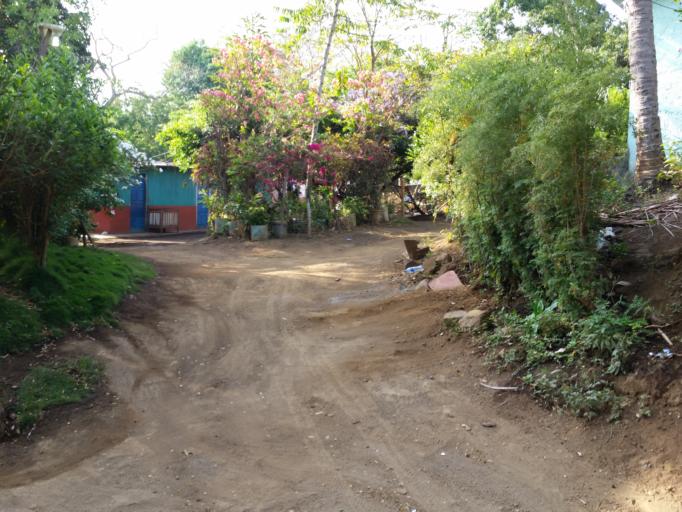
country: NI
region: Managua
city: Managua
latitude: 12.0852
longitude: -86.2603
